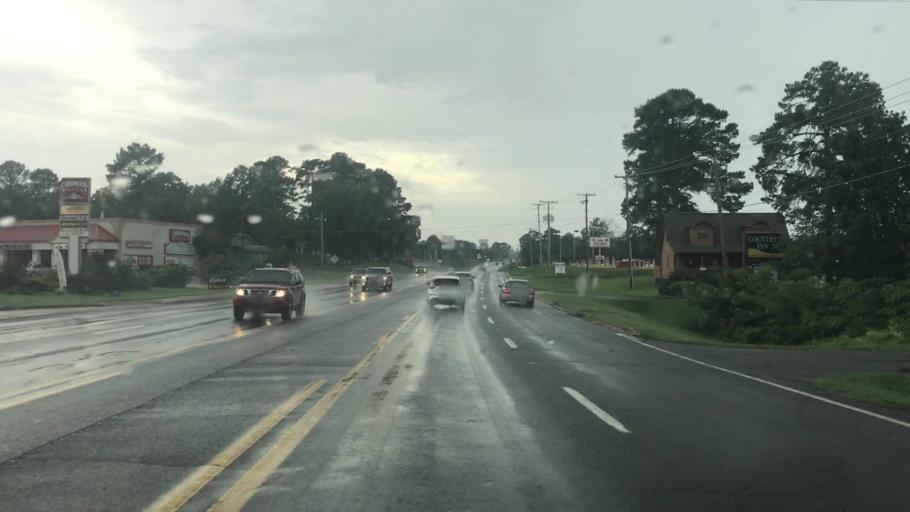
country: US
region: Arkansas
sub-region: Garland County
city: Rockwell
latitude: 34.4715
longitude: -93.1280
